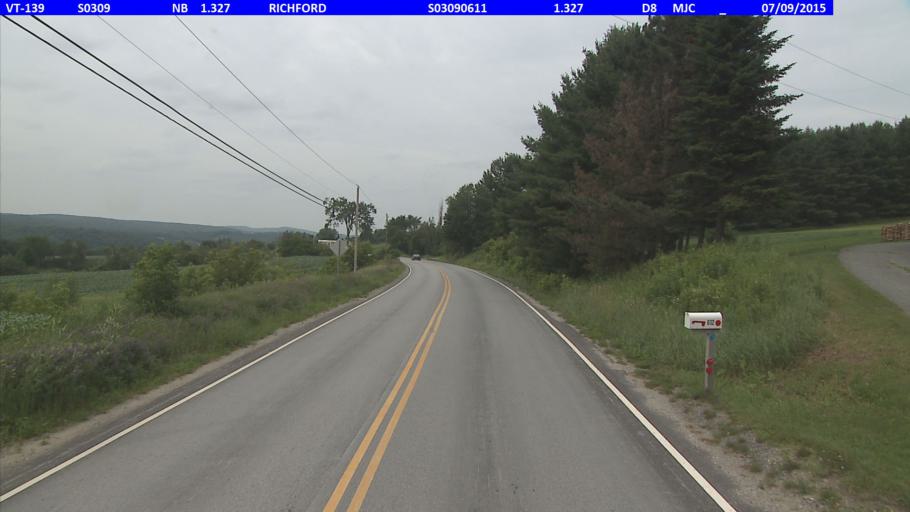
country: US
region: Vermont
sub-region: Franklin County
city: Richford
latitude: 45.0073
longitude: -72.6602
